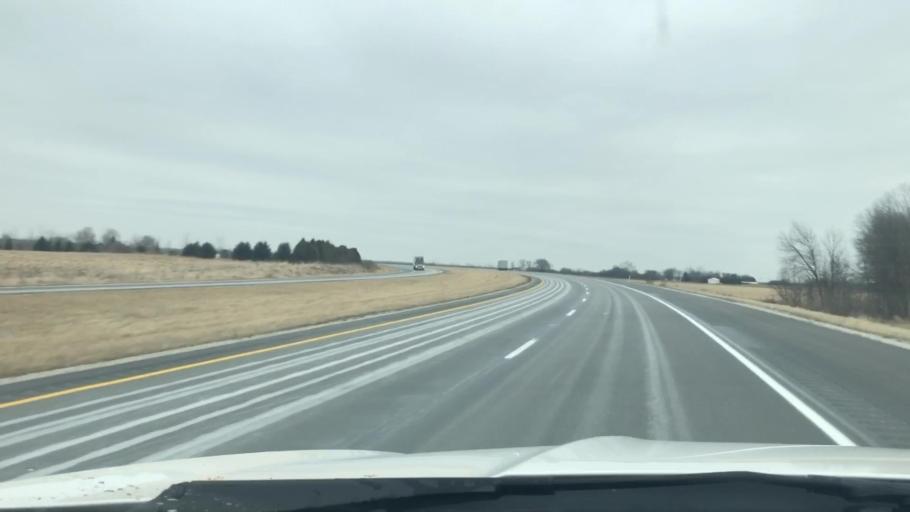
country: US
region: Indiana
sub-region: Cass County
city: Walton
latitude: 40.7367
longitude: -86.2707
